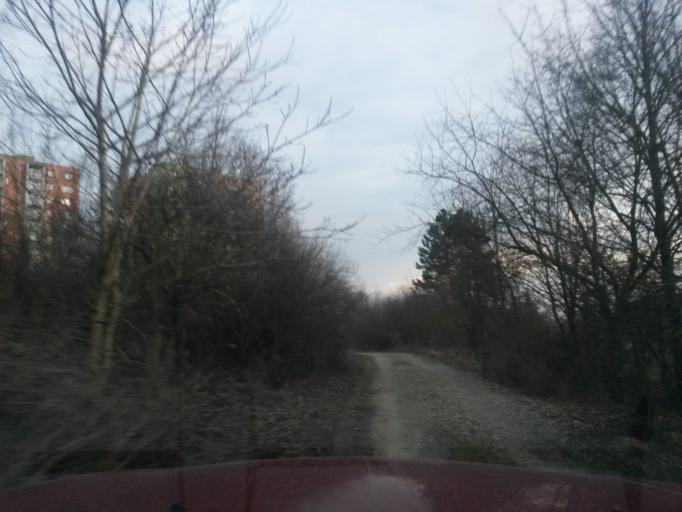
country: SK
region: Kosicky
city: Kosice
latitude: 48.7616
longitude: 21.2586
